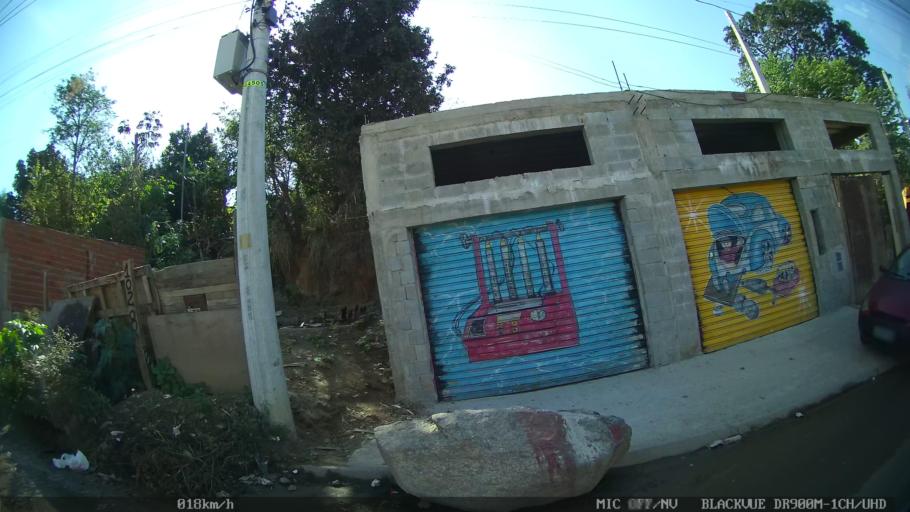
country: BR
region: Sao Paulo
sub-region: Campinas
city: Campinas
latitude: -22.9464
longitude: -47.0822
